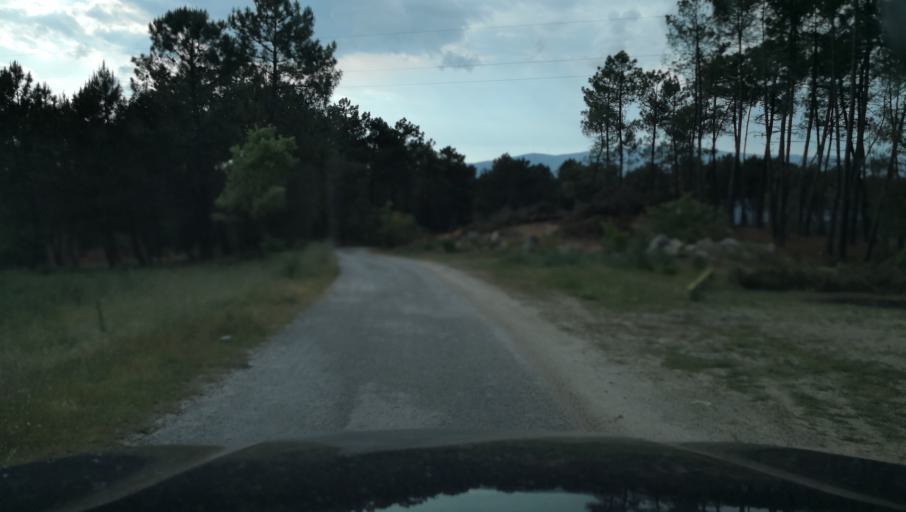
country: PT
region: Vila Real
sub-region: Vila Real
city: Vila Real
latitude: 41.3204
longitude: -7.6888
